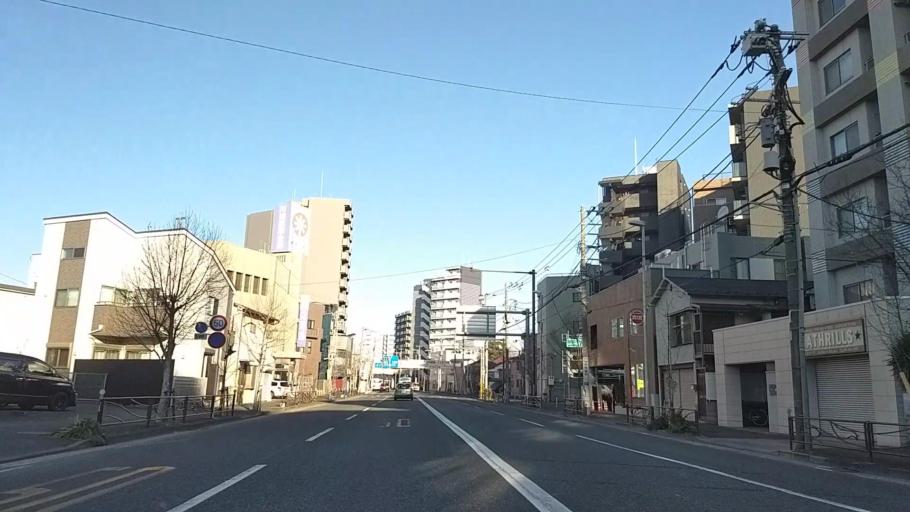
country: JP
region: Kanagawa
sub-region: Kawasaki-shi
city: Kawasaki
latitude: 35.5339
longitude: 139.6891
